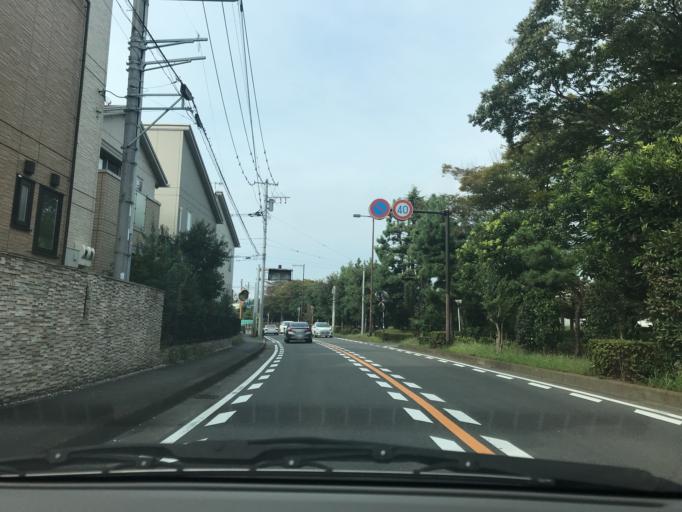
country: JP
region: Kanagawa
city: Fujisawa
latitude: 35.3364
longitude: 139.4691
